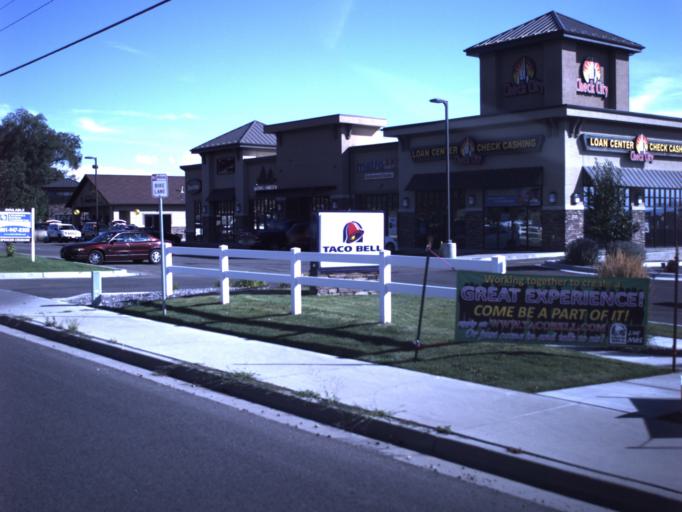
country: US
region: Utah
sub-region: Utah County
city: Lindon
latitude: 40.3490
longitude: -111.7284
